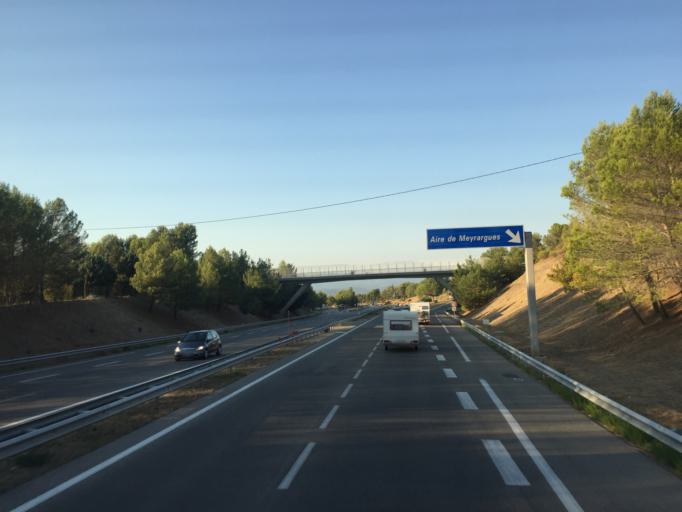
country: FR
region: Provence-Alpes-Cote d'Azur
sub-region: Departement des Bouches-du-Rhone
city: Venelles
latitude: 43.6283
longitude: 5.4931
